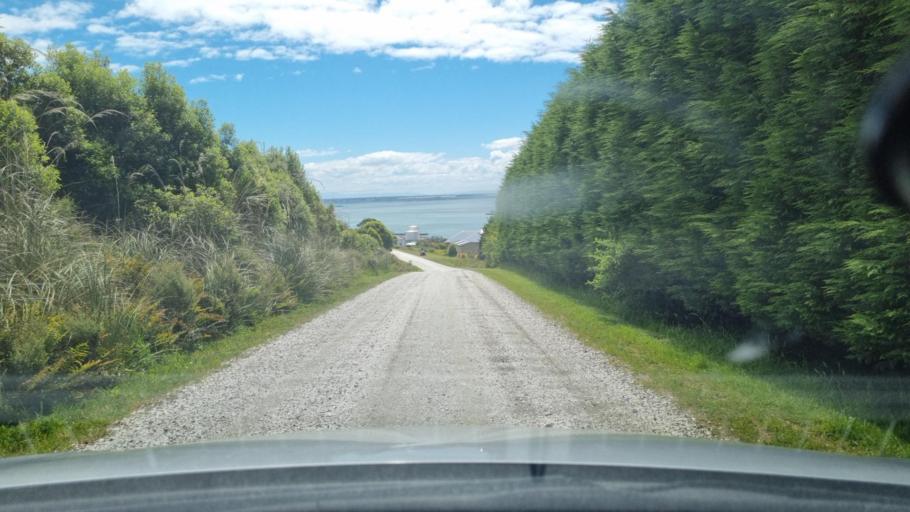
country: NZ
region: Southland
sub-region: Invercargill City
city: Bluff
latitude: -46.6096
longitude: 168.3520
